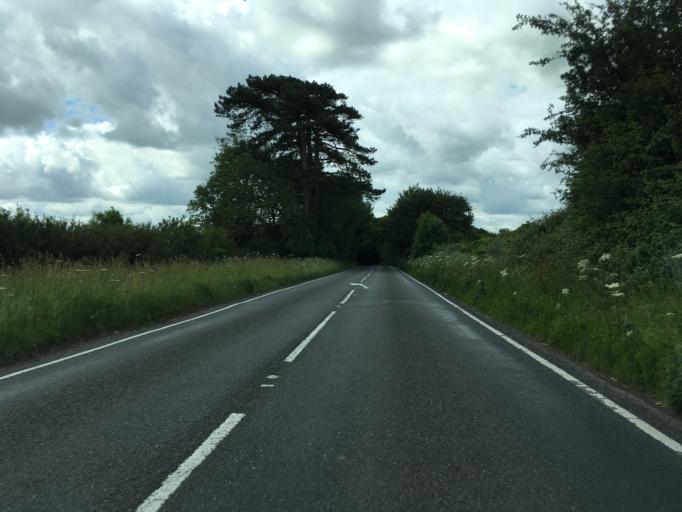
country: GB
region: England
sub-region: Oxfordshire
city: Shipton under Wychwood
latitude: 51.8921
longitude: -1.5642
